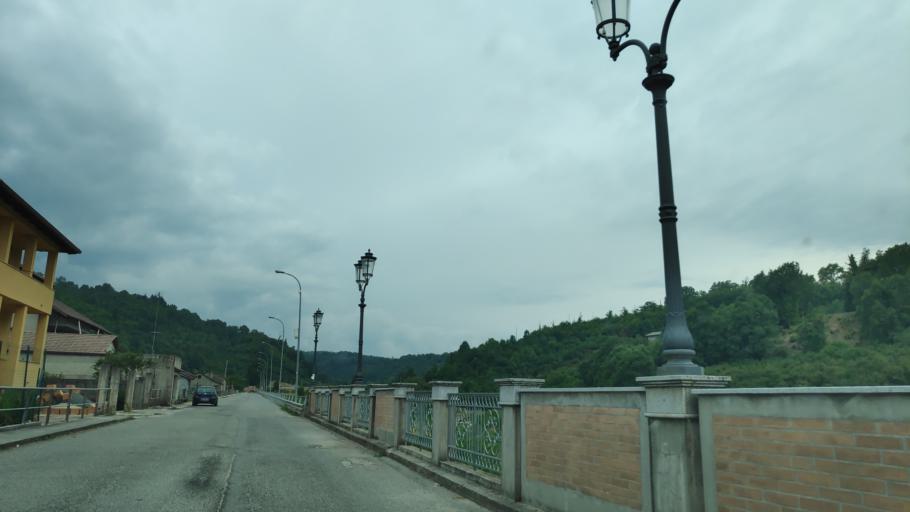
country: IT
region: Calabria
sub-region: Provincia di Catanzaro
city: Cardinale
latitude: 38.6415
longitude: 16.3846
